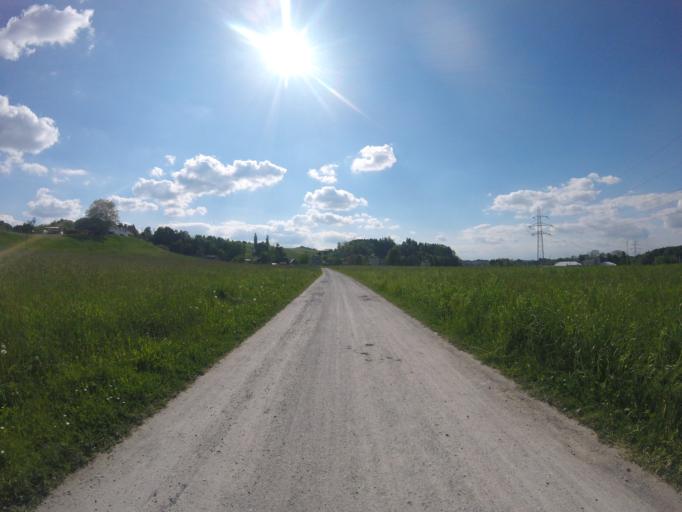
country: CH
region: Saint Gallen
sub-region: Wahlkreis Wil
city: Flawil
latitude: 47.4062
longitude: 9.2150
